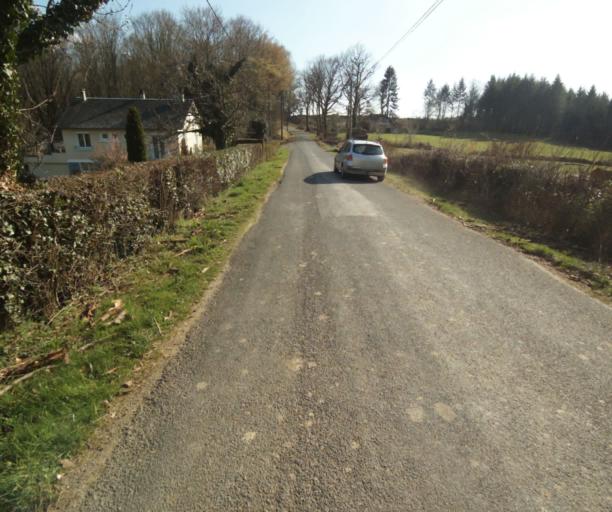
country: FR
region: Limousin
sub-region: Departement de la Correze
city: Saint-Mexant
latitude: 45.3239
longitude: 1.6254
